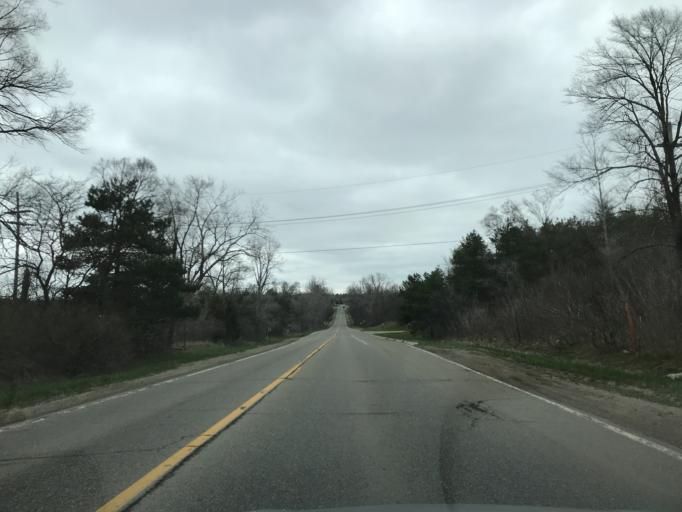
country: US
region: Michigan
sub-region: Oakland County
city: South Lyon
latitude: 42.5112
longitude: -83.6898
